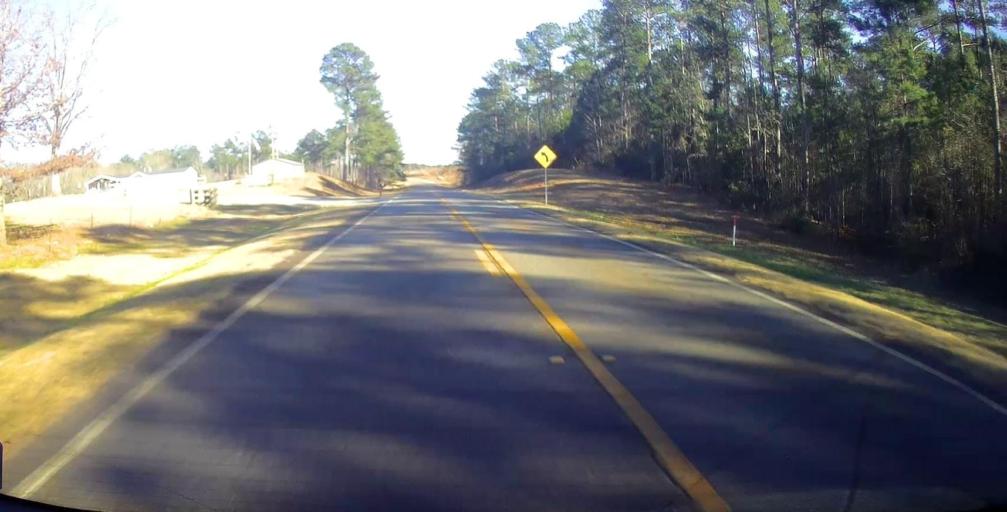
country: US
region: Georgia
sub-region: Talbot County
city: Sardis
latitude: 32.7871
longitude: -84.6413
